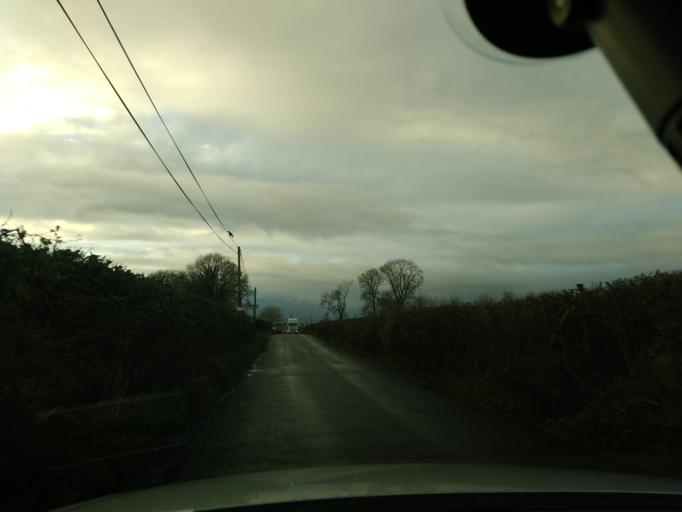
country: IE
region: Munster
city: Thurles
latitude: 52.6319
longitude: -7.7870
